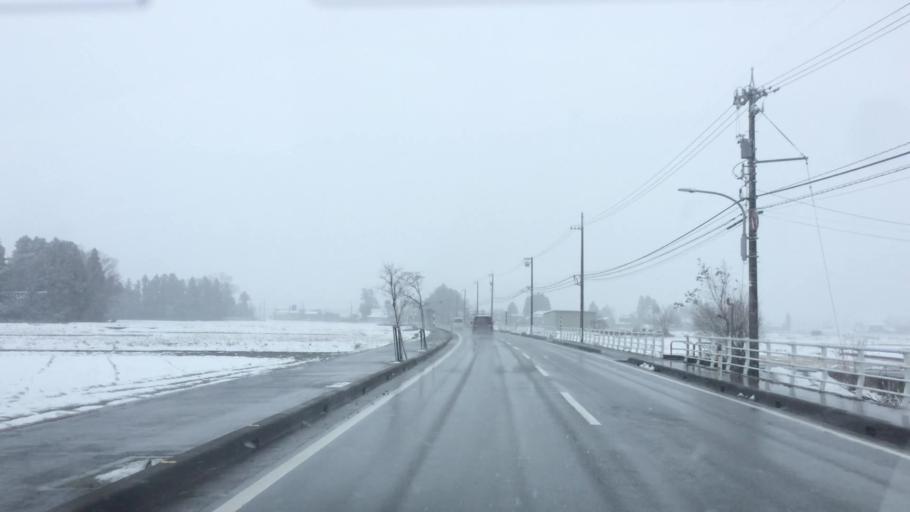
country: JP
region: Toyama
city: Toyama-shi
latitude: 36.6300
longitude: 137.2245
